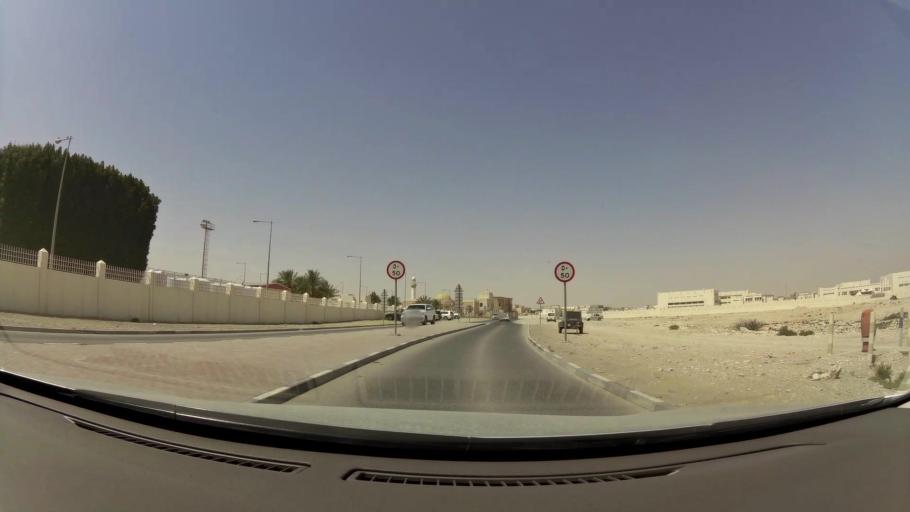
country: QA
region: Baladiyat ar Rayyan
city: Ar Rayyan
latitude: 25.2377
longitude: 51.4039
